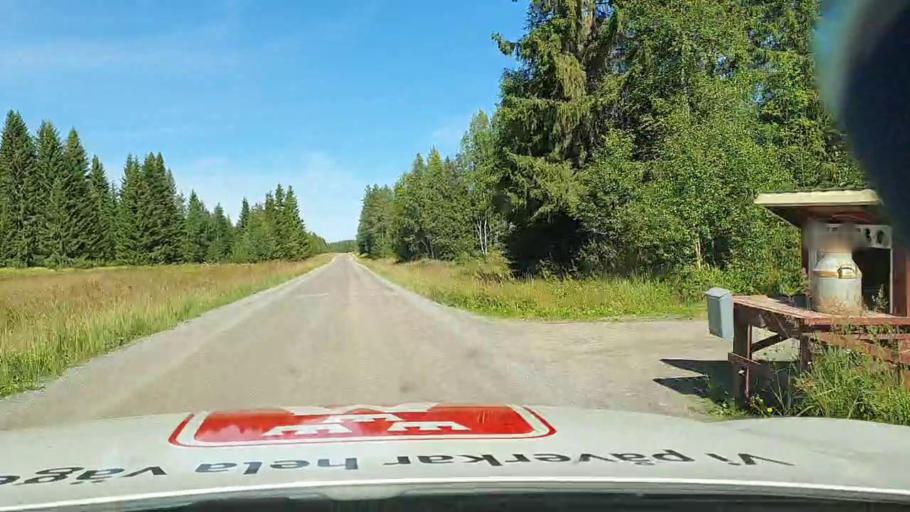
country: SE
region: Jaemtland
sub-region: Stroemsunds Kommun
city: Stroemsund
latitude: 63.6831
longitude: 15.3883
